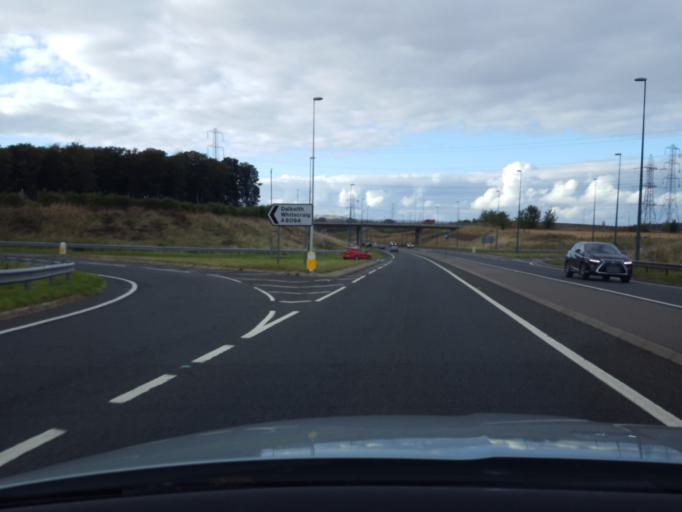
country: GB
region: Scotland
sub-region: Midlothian
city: Dalkeith
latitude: 55.9092
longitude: -3.0429
